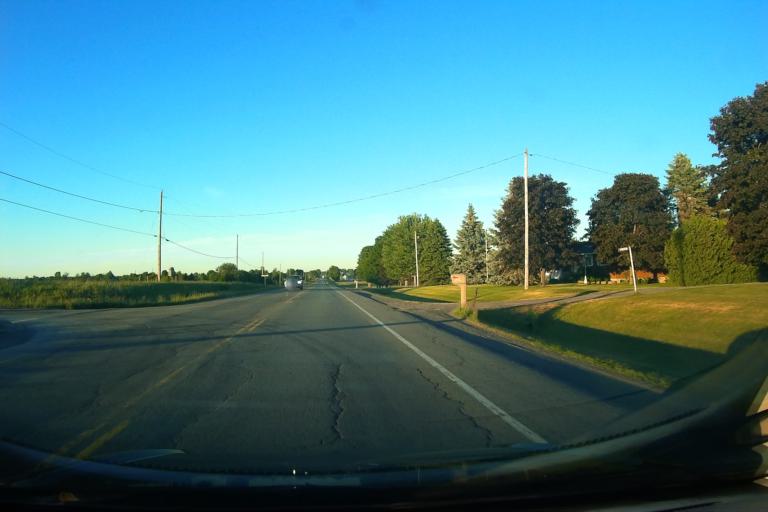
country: CA
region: Ontario
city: Prescott
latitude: 45.0759
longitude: -75.4025
